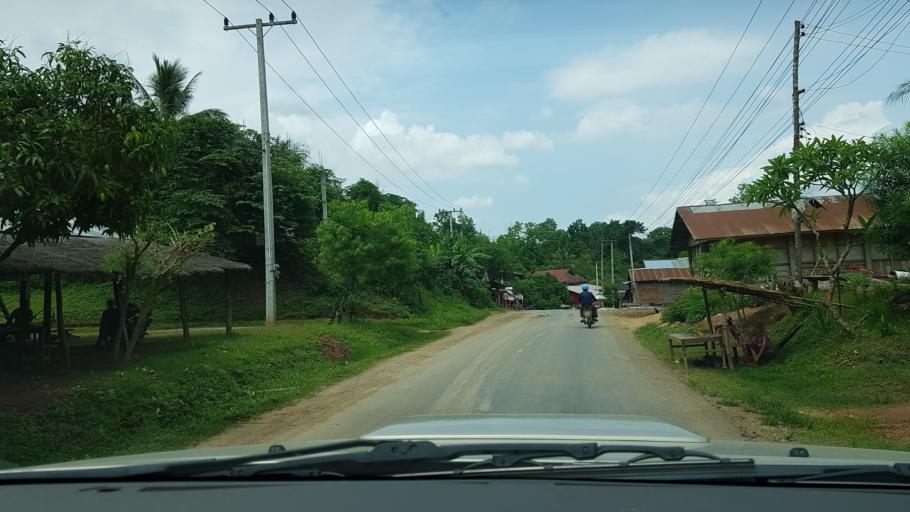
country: TH
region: Nan
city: Chaloem Phra Kiat
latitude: 20.0105
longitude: 101.3107
